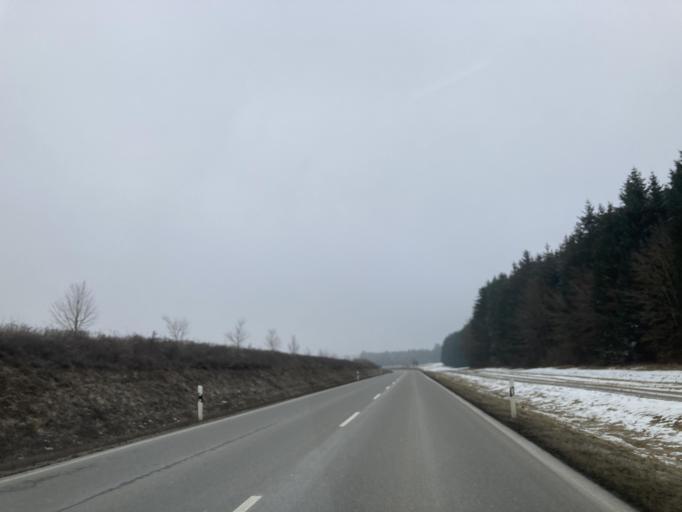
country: DE
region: Baden-Wuerttemberg
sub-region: Freiburg Region
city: Neuhausen ob Eck
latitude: 47.9642
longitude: 8.9384
